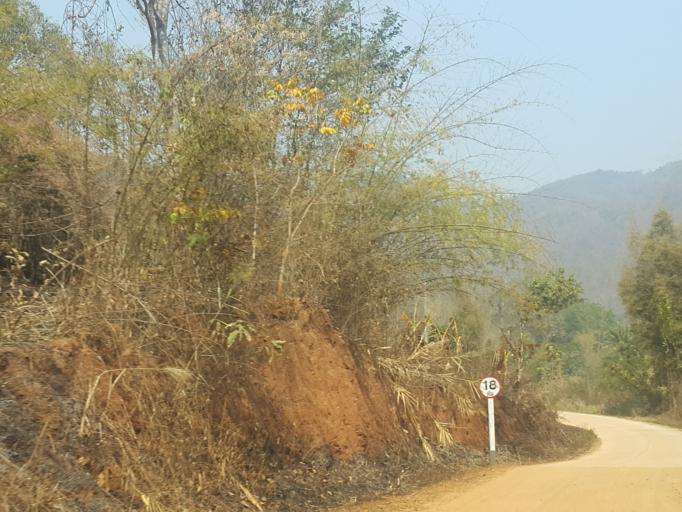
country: TH
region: Chiang Mai
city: Hang Dong
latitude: 18.7466
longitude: 98.8256
